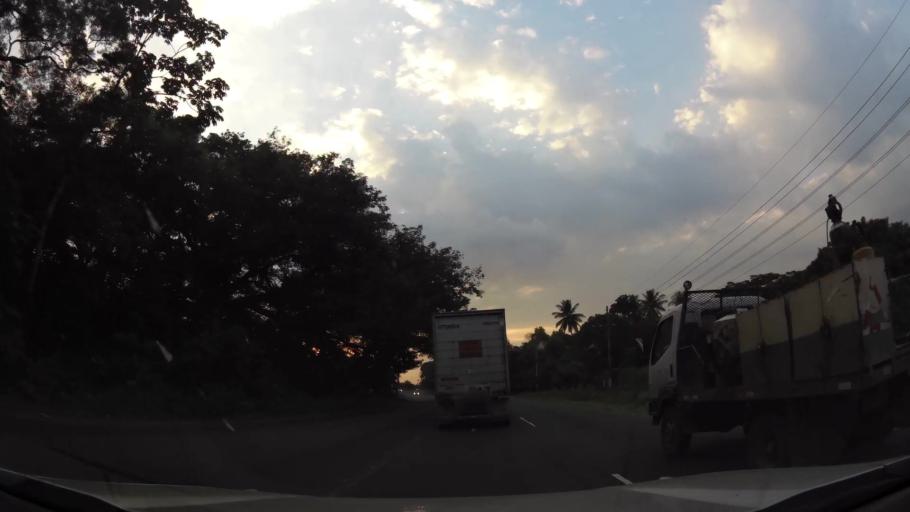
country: GT
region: Escuintla
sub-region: Municipio de La Democracia
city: La Democracia
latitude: 14.2668
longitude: -90.8919
